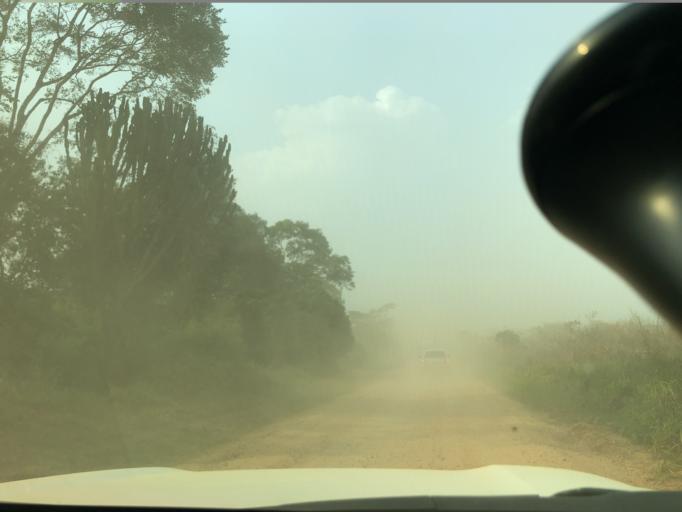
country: CD
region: Nord Kivu
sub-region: North Kivu
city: Butembo
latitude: 0.0995
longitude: 29.6404
